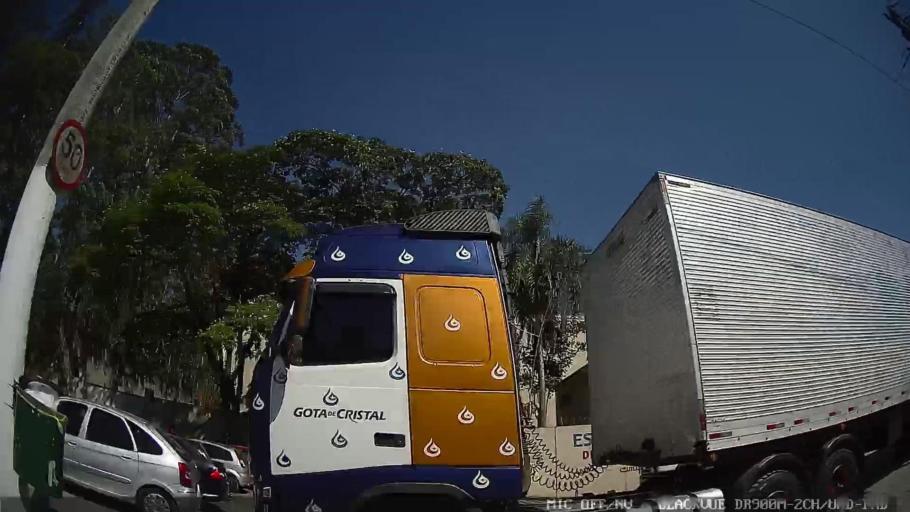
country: BR
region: Sao Paulo
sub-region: Sao Caetano Do Sul
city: Sao Caetano do Sul
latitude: -23.5736
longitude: -46.4750
